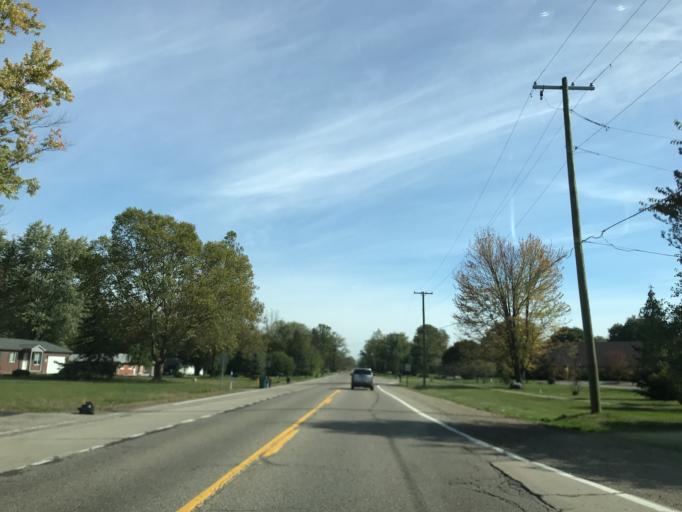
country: US
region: Michigan
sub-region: Oakland County
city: Farmington
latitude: 42.4709
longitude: -83.3274
